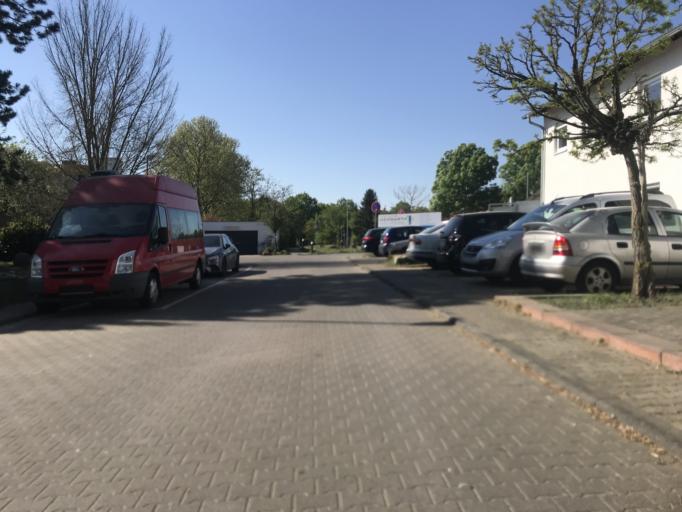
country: DE
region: Rheinland-Pfalz
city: Budenheim
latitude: 50.0259
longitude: 8.1963
